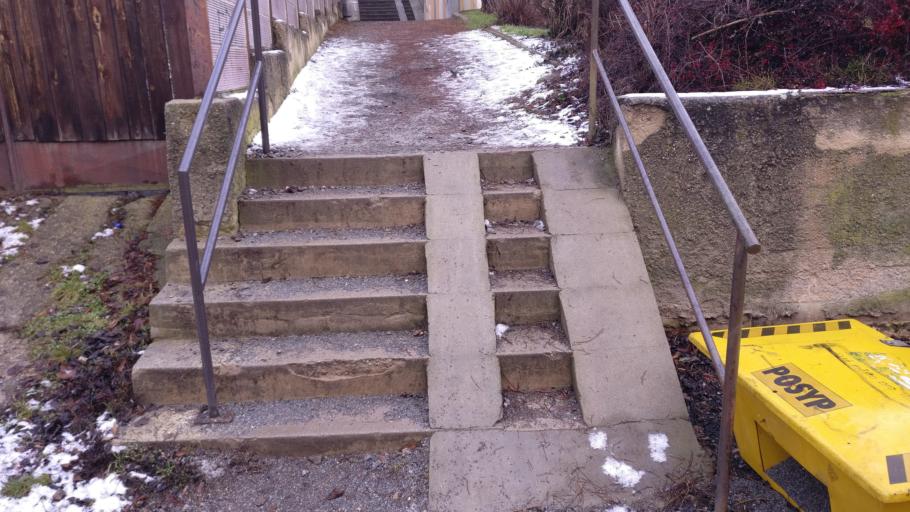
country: CZ
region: South Moravian
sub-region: Okres Brno-Venkov
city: Rosice
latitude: 49.1806
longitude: 16.3896
